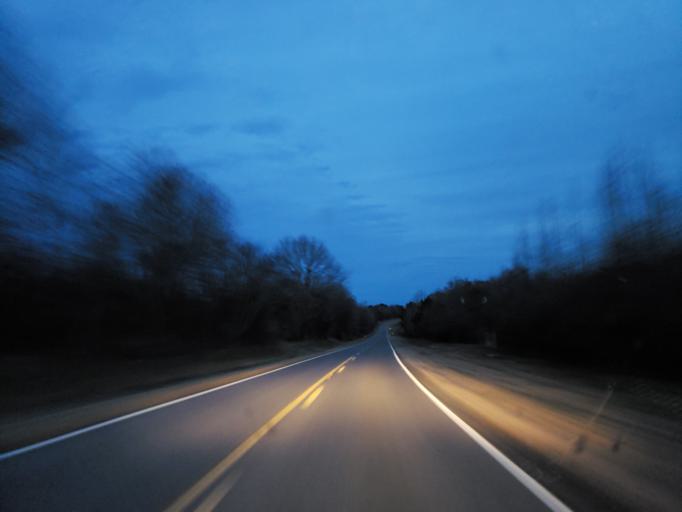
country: US
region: Alabama
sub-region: Greene County
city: Eutaw
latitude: 32.8965
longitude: -87.9592
